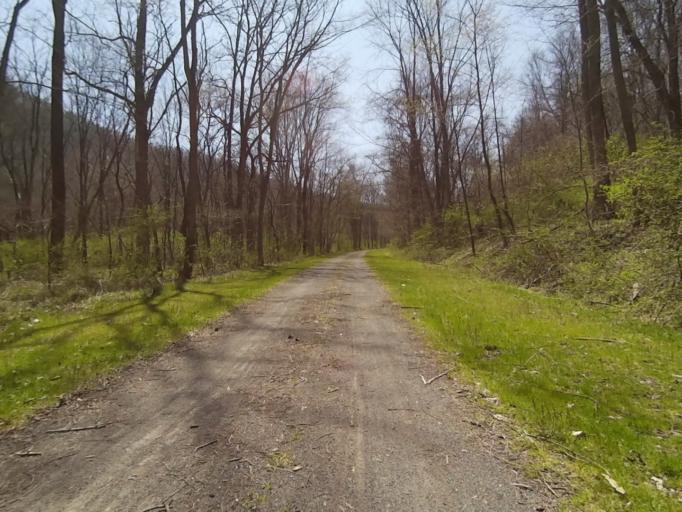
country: US
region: Pennsylvania
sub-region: Blair County
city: Williamsburg
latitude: 40.4921
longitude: -78.1665
